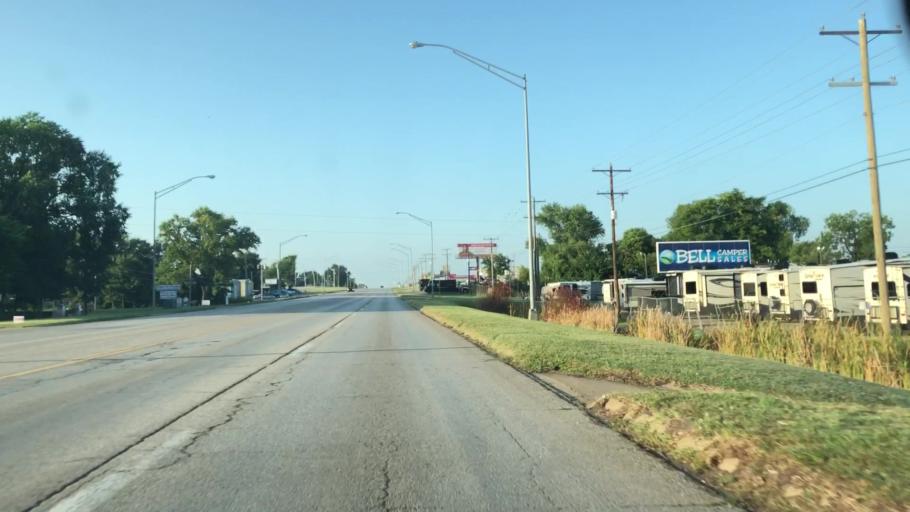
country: US
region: Oklahoma
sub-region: Washington County
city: Dewey
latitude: 36.7705
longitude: -95.9355
